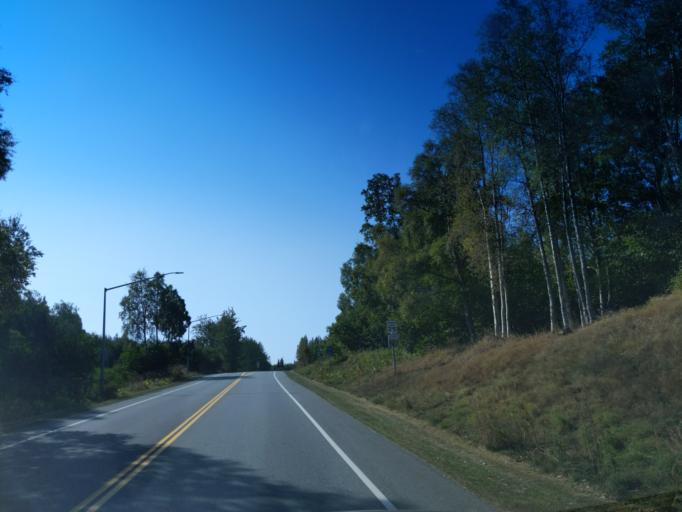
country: US
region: Alaska
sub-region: Anchorage Municipality
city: Anchorage
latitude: 61.1562
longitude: -150.0164
